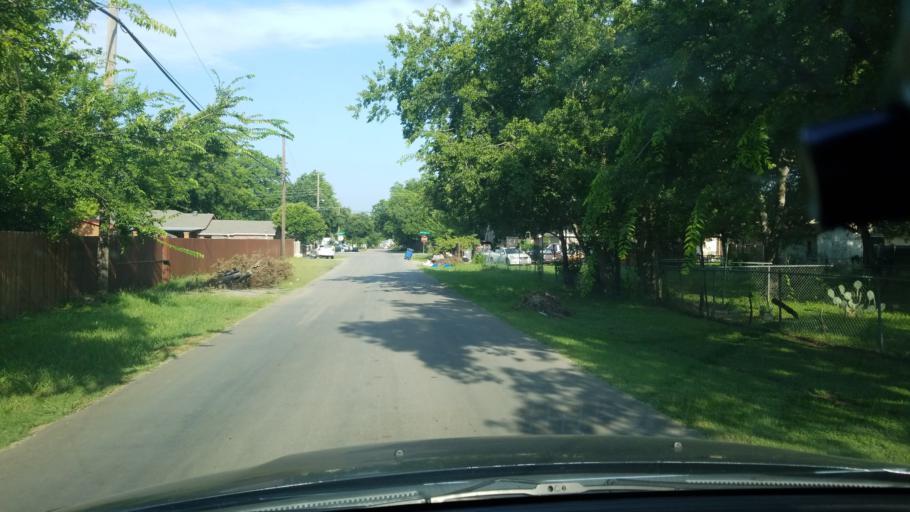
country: US
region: Texas
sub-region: Dallas County
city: Balch Springs
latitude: 32.7289
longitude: -96.6855
